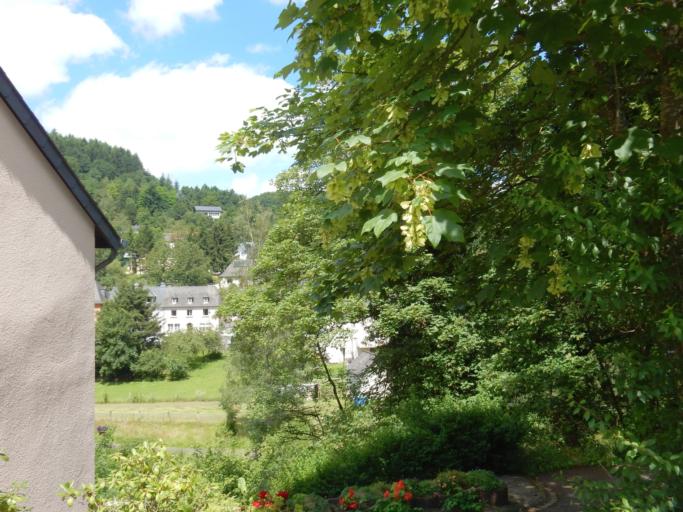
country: LU
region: Diekirch
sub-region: Canton de Wiltz
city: Wilwerwiltz
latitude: 49.9517
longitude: 6.0195
